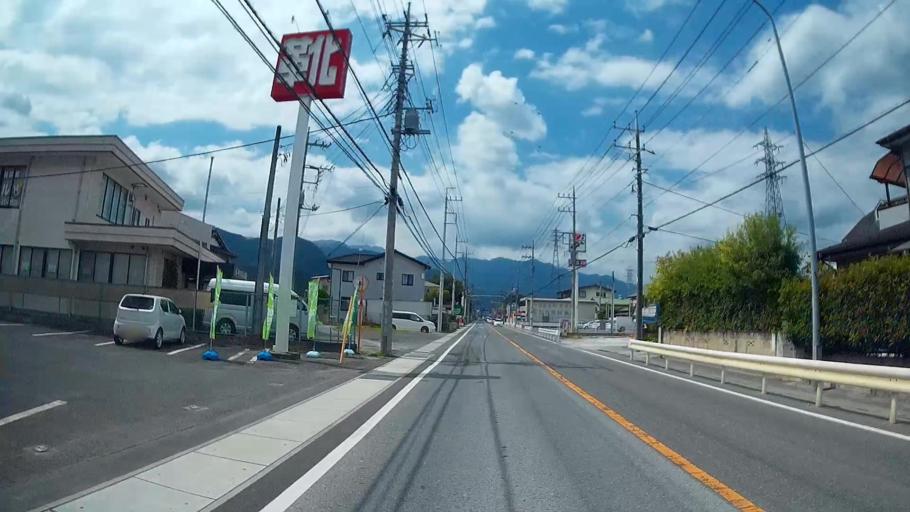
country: JP
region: Saitama
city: Chichibu
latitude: 35.9787
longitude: 139.0736
